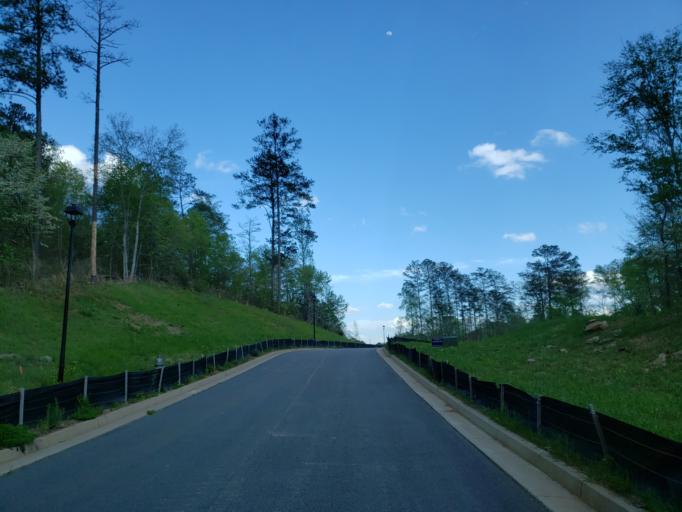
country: US
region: Georgia
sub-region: Fulton County
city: Roswell
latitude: 34.1105
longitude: -84.3915
